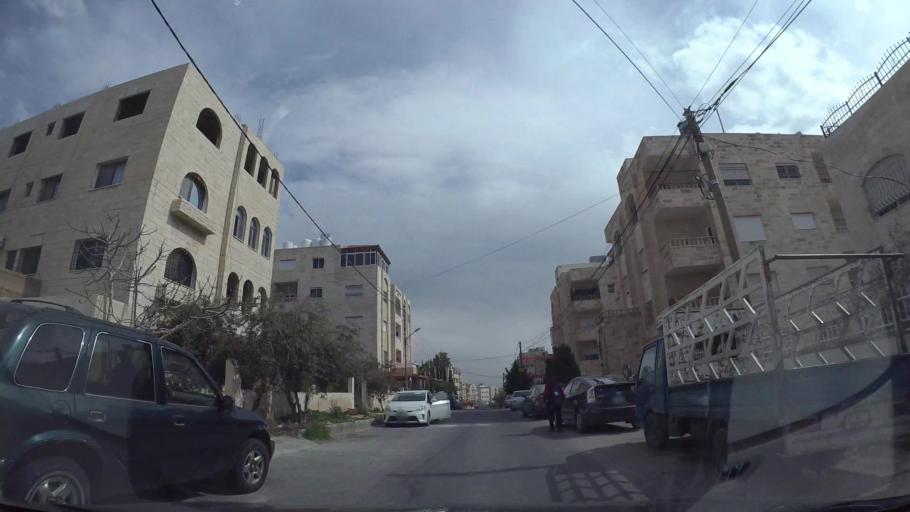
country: JO
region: Amman
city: Amman
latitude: 32.0007
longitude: 35.9372
